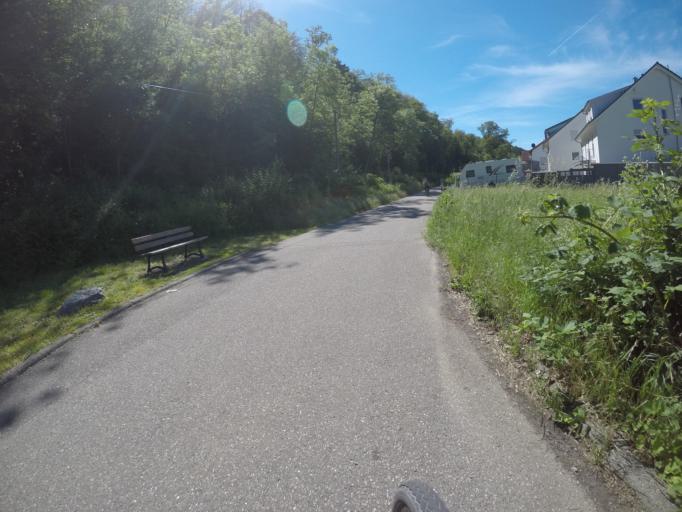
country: DE
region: Baden-Wuerttemberg
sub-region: Karlsruhe Region
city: Konigsbach-Stein
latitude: 48.9435
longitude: 8.6289
